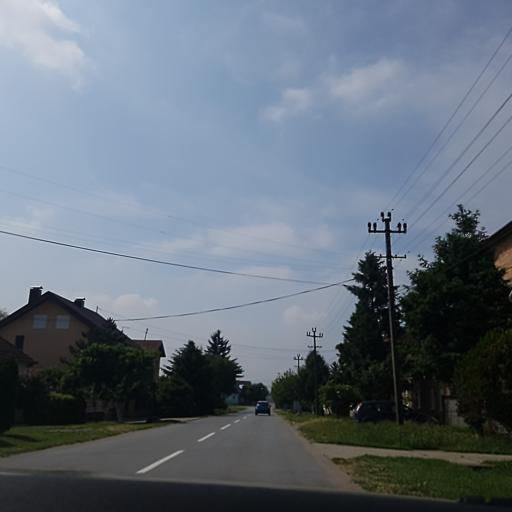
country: RS
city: Padina
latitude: 45.1205
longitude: 20.7218
